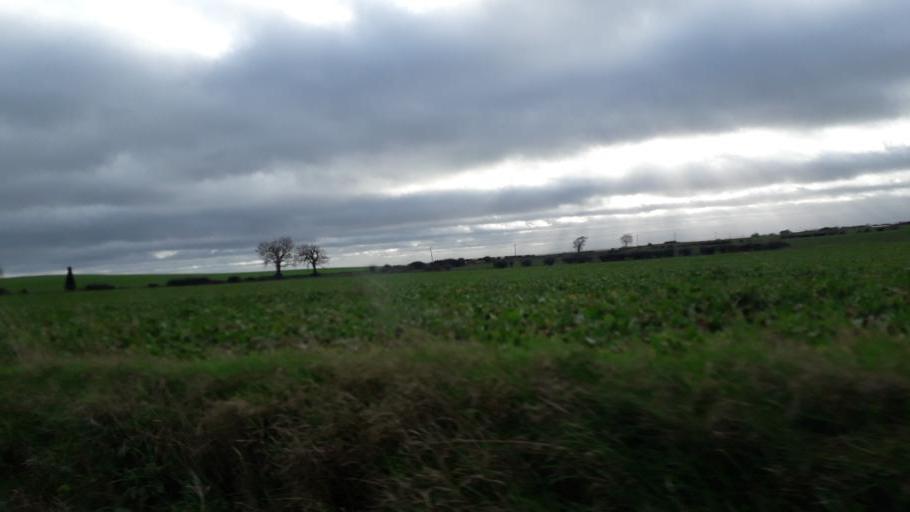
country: IE
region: Leinster
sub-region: Fingal County
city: Skerries
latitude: 53.5566
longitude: -6.1340
